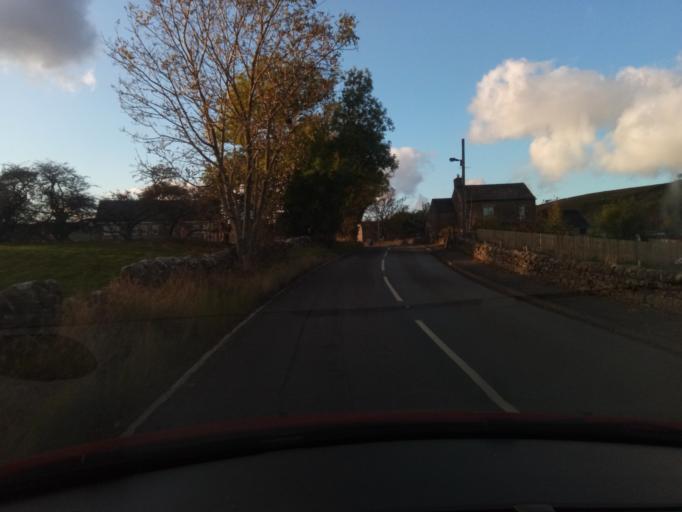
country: GB
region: England
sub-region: County Durham
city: Newbiggin
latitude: 54.7470
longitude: -2.2152
